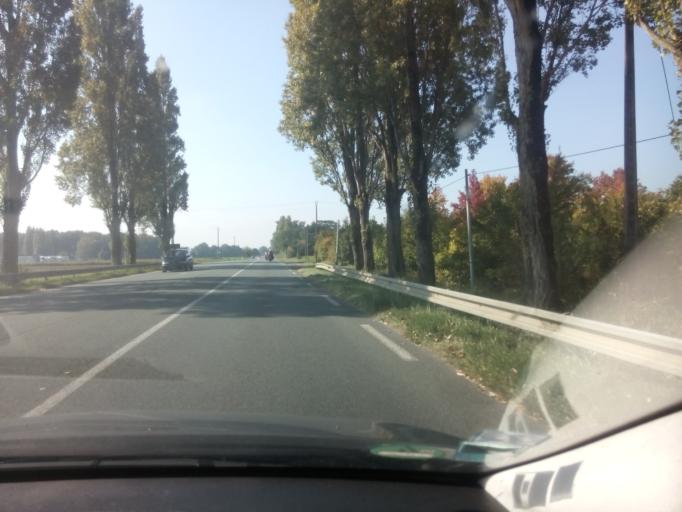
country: FR
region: Pays de la Loire
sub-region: Departement de Maine-et-Loire
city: Villeveque
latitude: 47.5364
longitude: -0.4097
